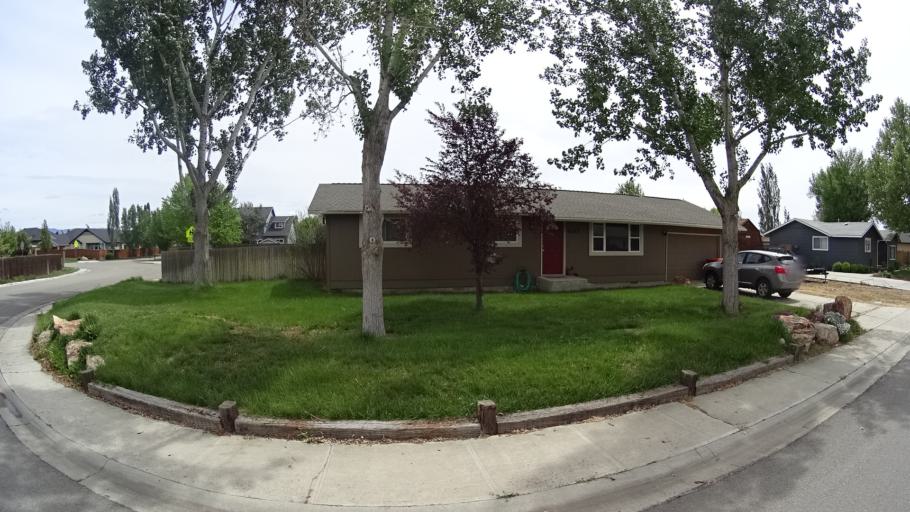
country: US
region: Idaho
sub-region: Ada County
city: Meridian
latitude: 43.5438
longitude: -116.3251
